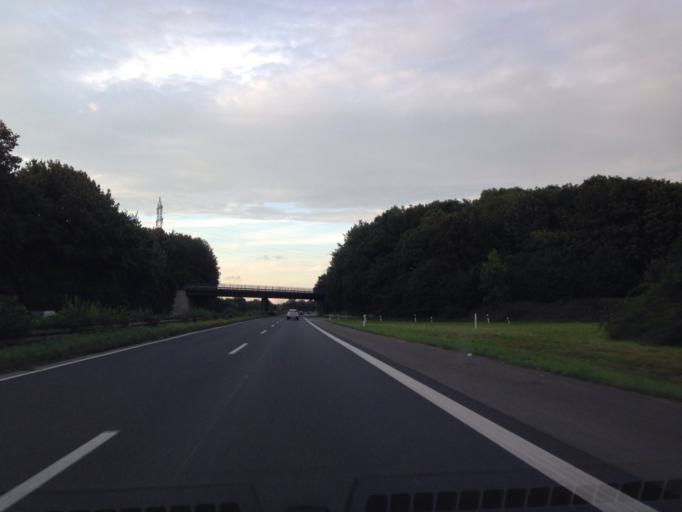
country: DE
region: North Rhine-Westphalia
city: Erkelenz
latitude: 51.0798
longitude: 6.3368
